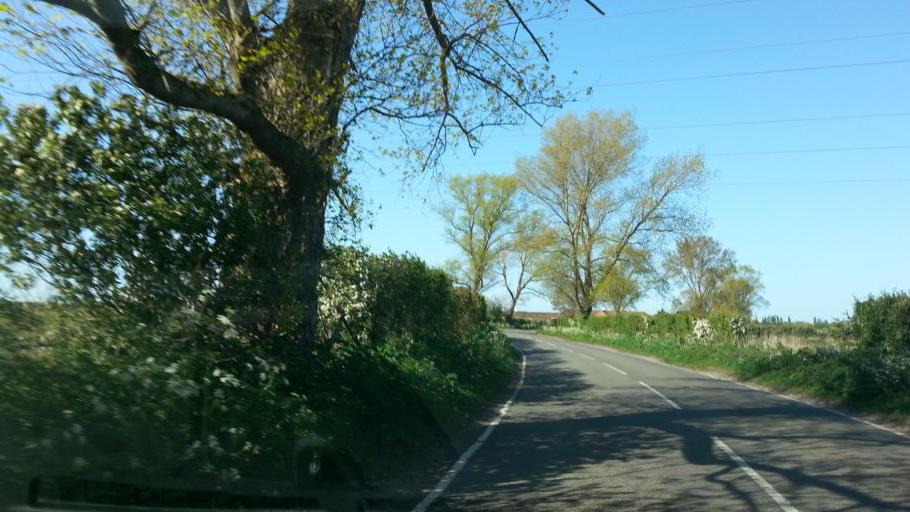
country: GB
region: England
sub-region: Lincolnshire
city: Great Gonerby
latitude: 52.9732
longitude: -0.6835
